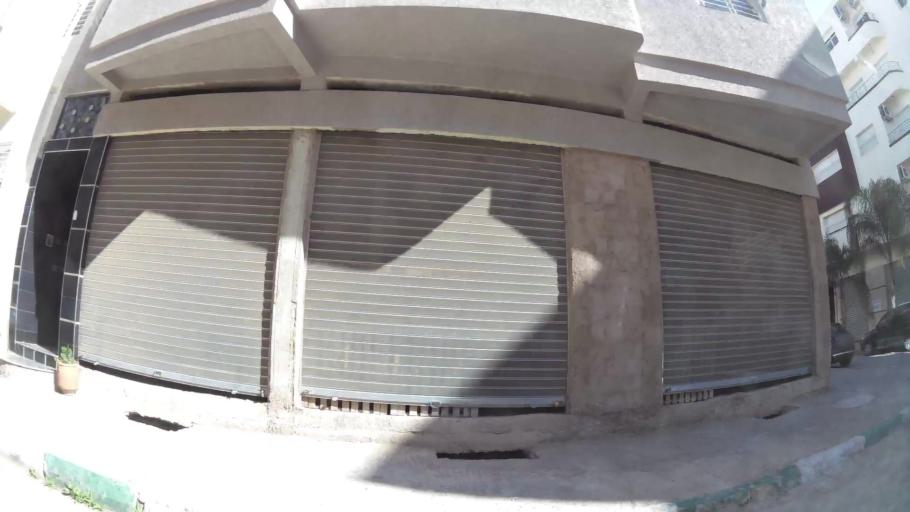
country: MA
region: Fes-Boulemane
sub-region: Fes
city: Fes
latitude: 34.0006
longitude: -5.0098
